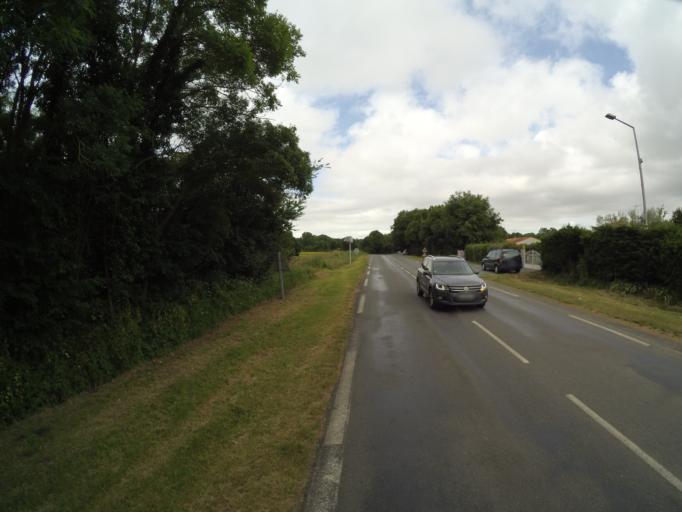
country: FR
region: Poitou-Charentes
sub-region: Departement de la Charente-Maritime
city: Saint-Laurent-de-la-Pree
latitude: 45.9932
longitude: -1.0308
